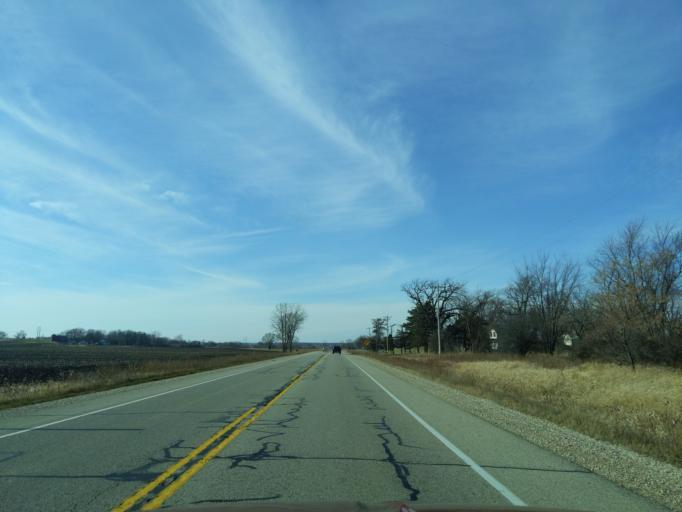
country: US
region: Wisconsin
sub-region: Walworth County
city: Whitewater
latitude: 42.8080
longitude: -88.6735
